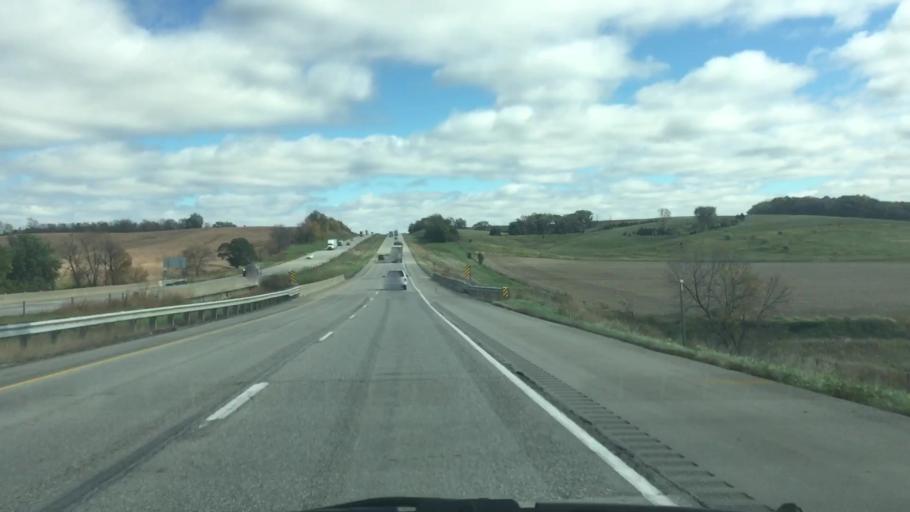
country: US
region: Iowa
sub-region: Poweshiek County
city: Grinnell
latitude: 41.6950
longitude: -92.8450
